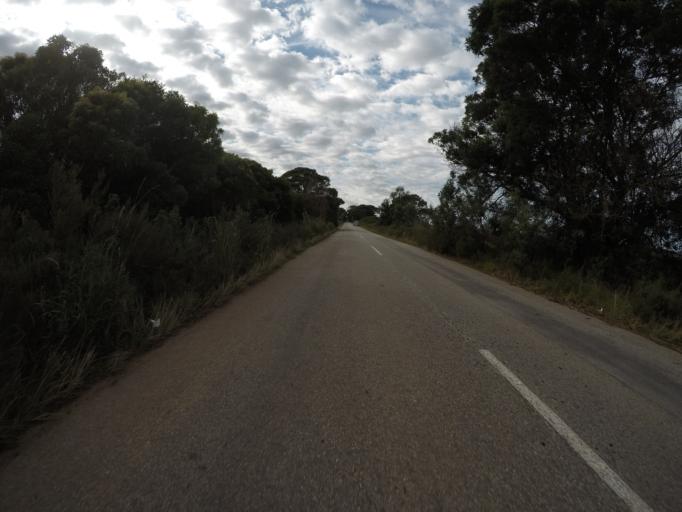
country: ZA
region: Eastern Cape
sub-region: Cacadu District Municipality
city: Kareedouw
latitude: -34.0455
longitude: 24.4475
